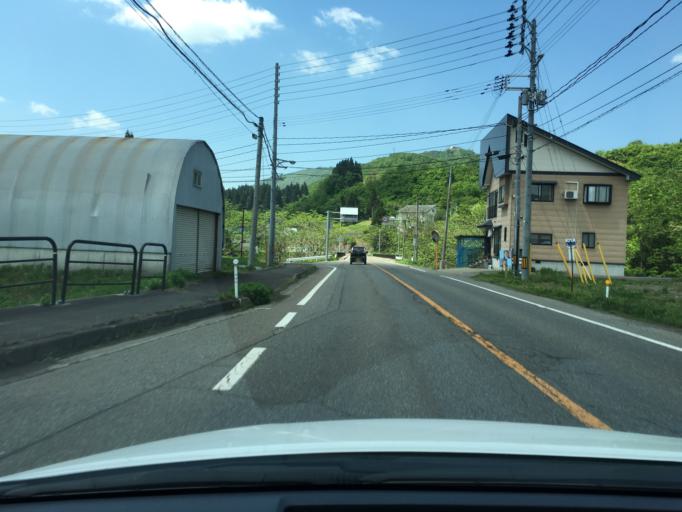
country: JP
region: Niigata
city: Tochio-honcho
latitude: 37.3342
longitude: 139.0308
